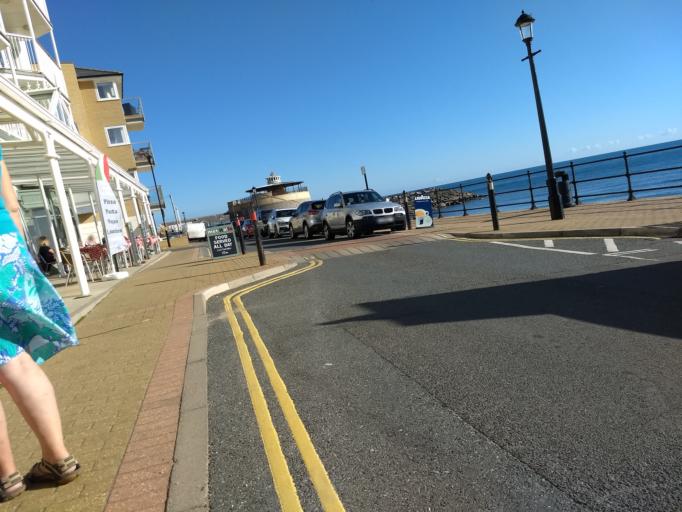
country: GB
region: England
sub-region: Isle of Wight
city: Ventnor
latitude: 50.5933
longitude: -1.2074
